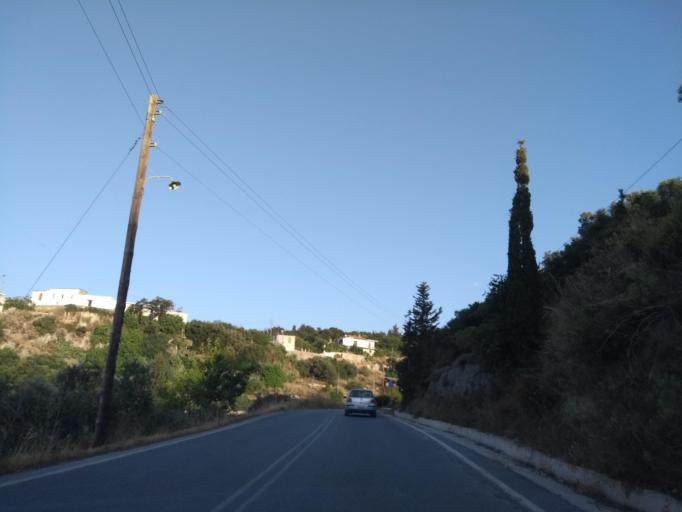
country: GR
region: Crete
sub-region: Nomos Chanias
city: Kalivai
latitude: 35.4356
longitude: 24.1758
